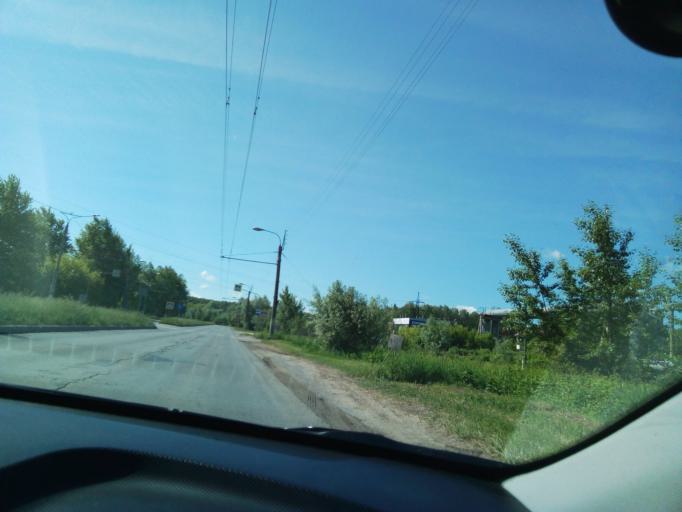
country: RU
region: Chuvashia
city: Novocheboksarsk
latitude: 56.0883
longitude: 47.5017
